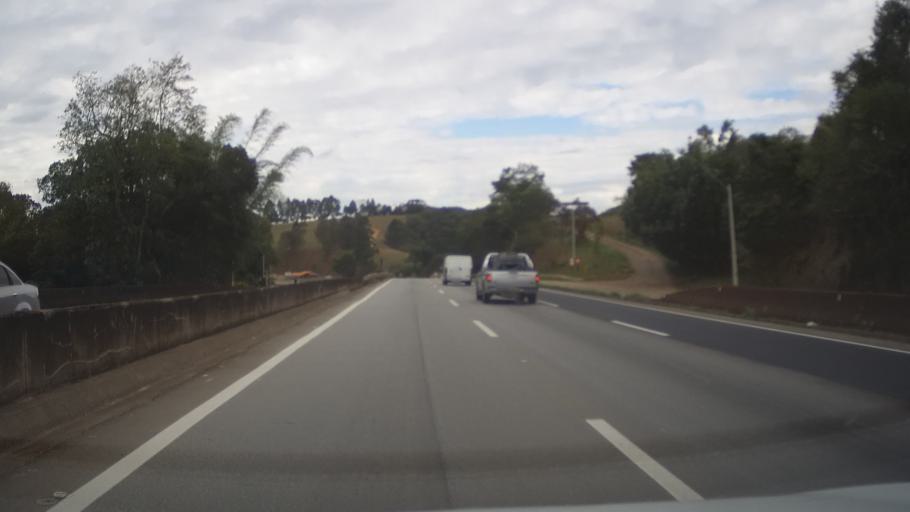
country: BR
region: Minas Gerais
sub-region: Itauna
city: Itauna
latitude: -20.3429
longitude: -44.4409
